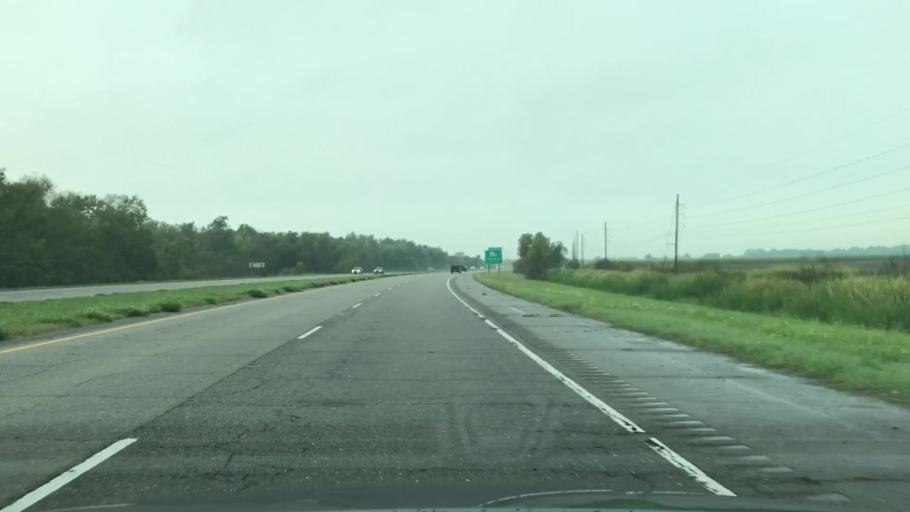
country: US
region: Louisiana
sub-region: Lafourche Parish
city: Mathews
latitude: 29.7199
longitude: -90.5615
